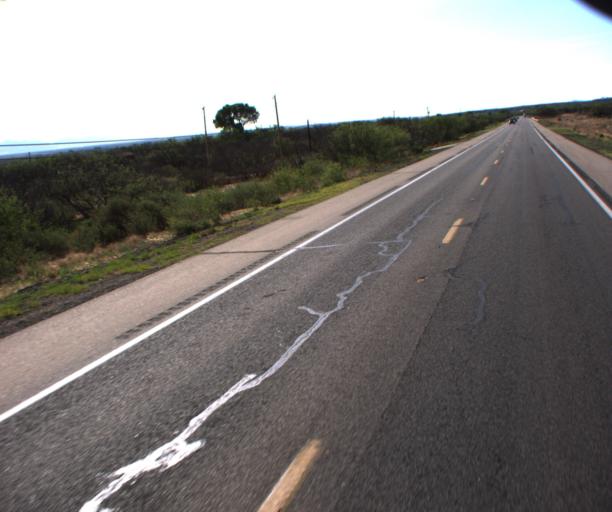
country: US
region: Arizona
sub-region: Cochise County
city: Saint David
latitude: 31.9162
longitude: -110.2632
